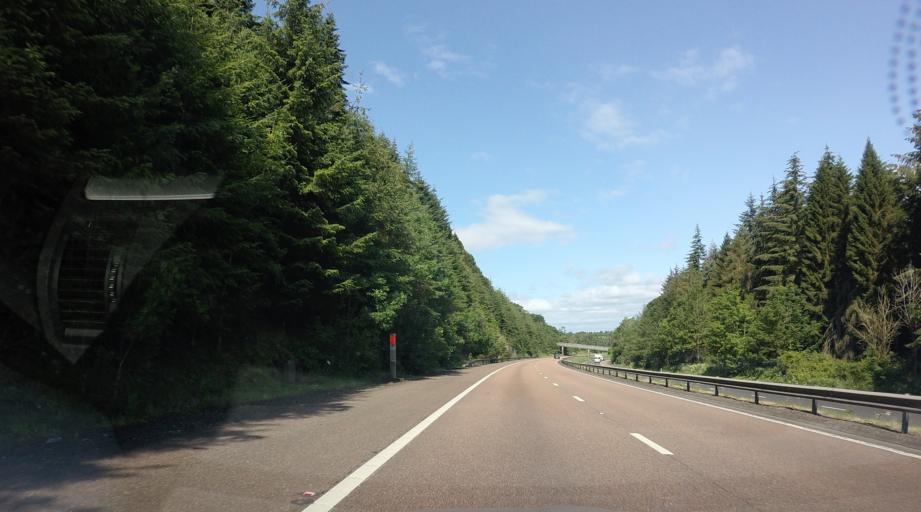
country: GB
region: Scotland
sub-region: Perth and Kinross
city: Bridge of Earn
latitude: 56.3201
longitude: -3.3866
